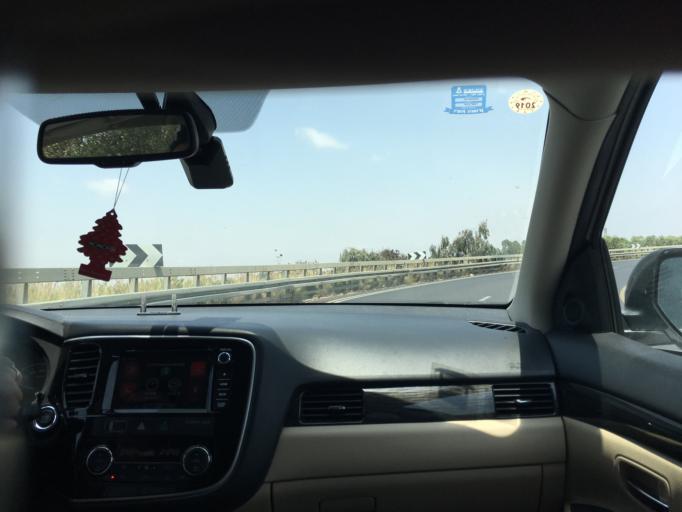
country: IL
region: Tel Aviv
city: Herzliyya
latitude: 32.1416
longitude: 34.8073
